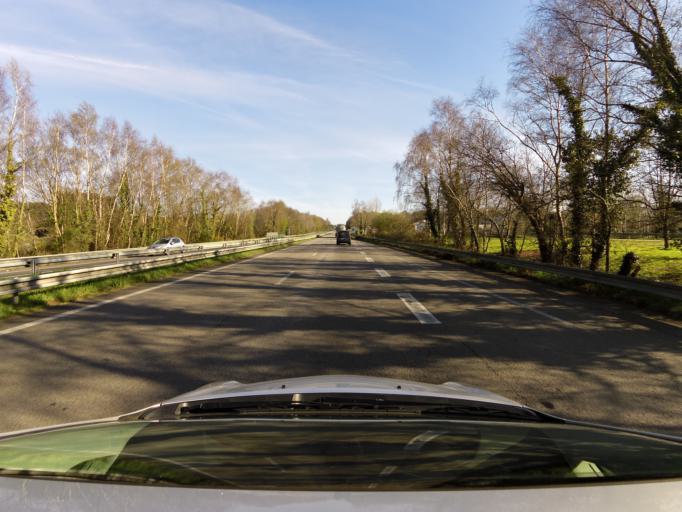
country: FR
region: Brittany
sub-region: Departement du Morbihan
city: Kervignac
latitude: 47.7896
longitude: -3.2420
